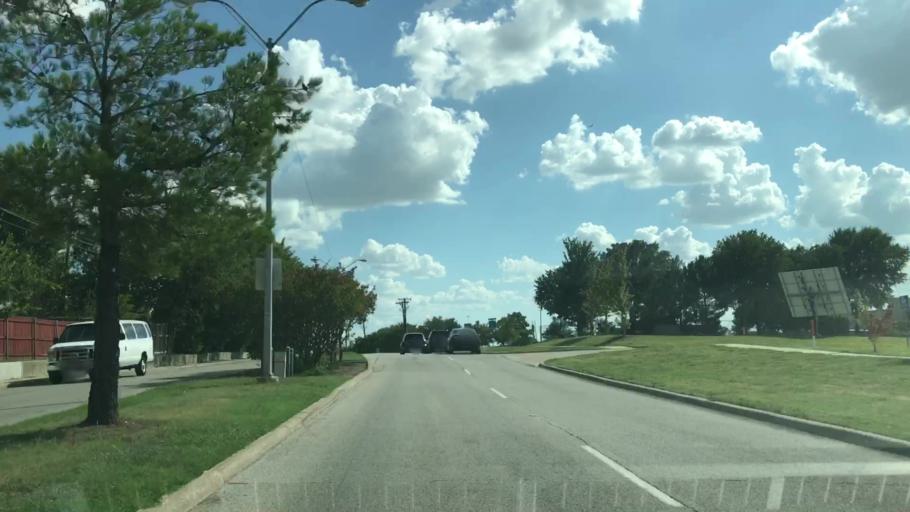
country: US
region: Texas
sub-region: Dallas County
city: Irving
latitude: 32.8455
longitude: -97.0090
